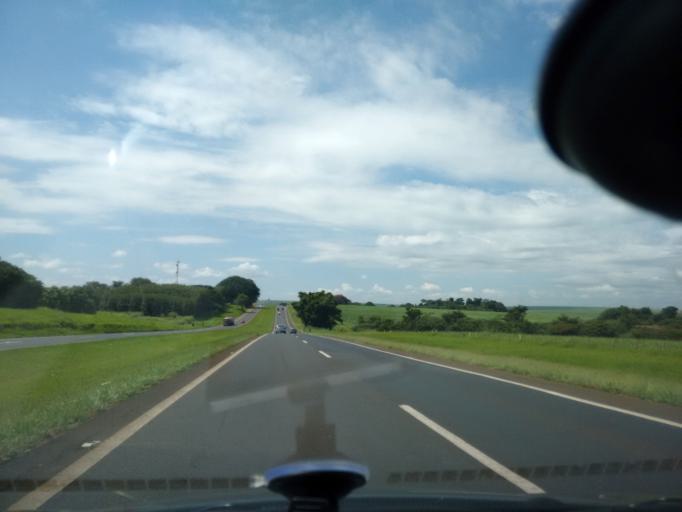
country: BR
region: Sao Paulo
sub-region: Araraquara
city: Araraquara
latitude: -21.8698
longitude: -48.1070
